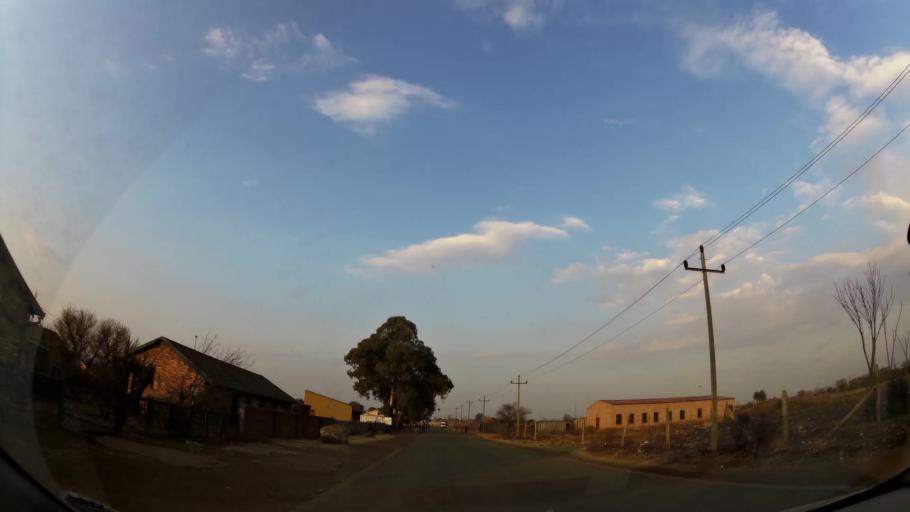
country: ZA
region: Gauteng
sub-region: City of Johannesburg Metropolitan Municipality
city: Orange Farm
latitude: -26.5464
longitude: 27.8758
